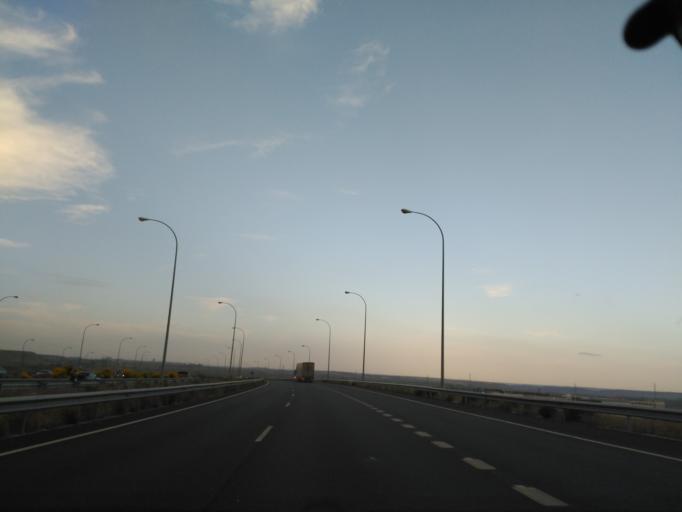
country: ES
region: Madrid
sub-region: Provincia de Madrid
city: Villaverde
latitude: 40.3259
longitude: -3.6882
